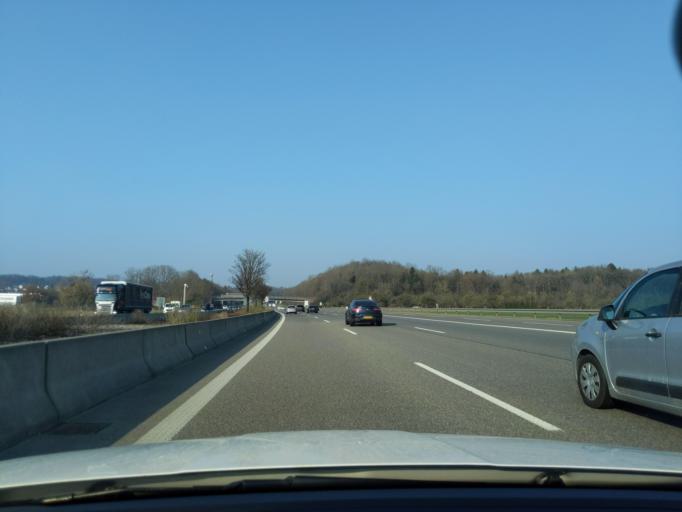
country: DE
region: Baden-Wuerttemberg
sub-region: Regierungsbezirk Stuttgart
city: Leinfelden-Echterdingen
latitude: 48.7100
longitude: 9.1349
